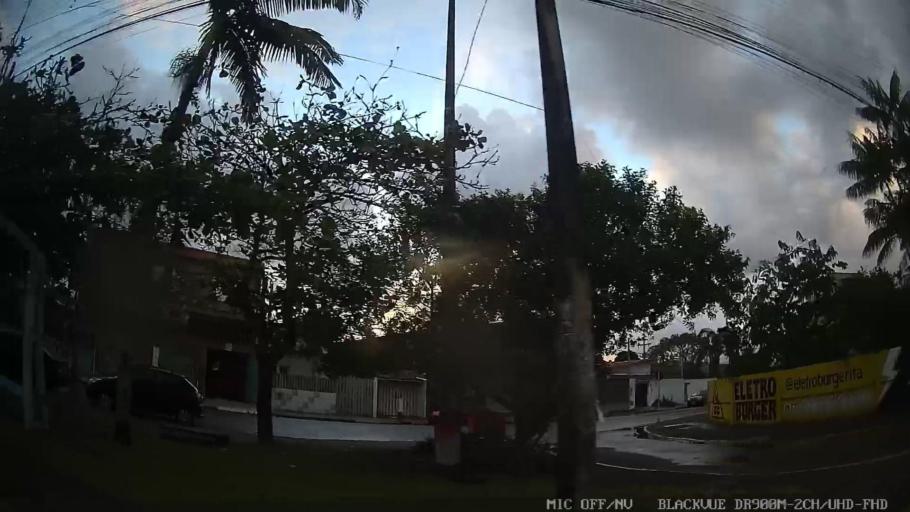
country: BR
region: Sao Paulo
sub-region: Itanhaem
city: Itanhaem
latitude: -24.1772
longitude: -46.7880
